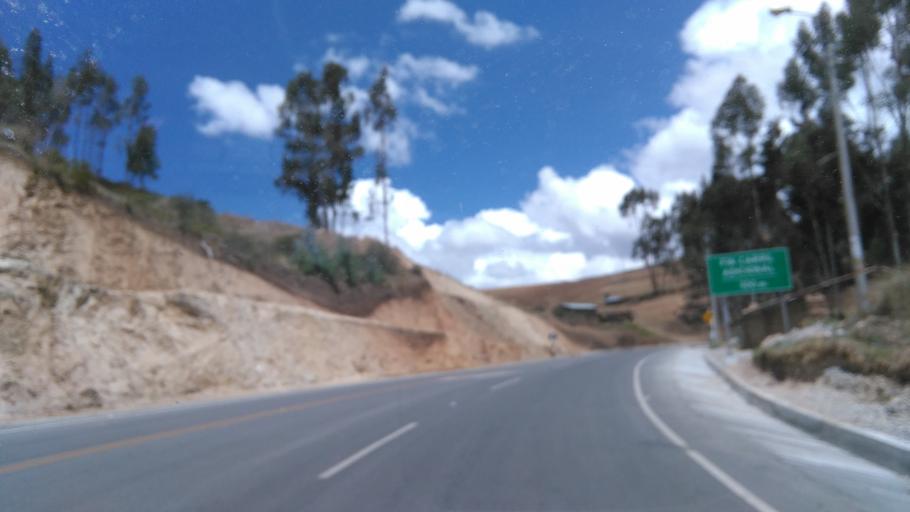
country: PE
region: Apurimac
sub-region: Provincia de Andahuaylas
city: San Jeronimo
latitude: -13.6881
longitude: -73.3573
